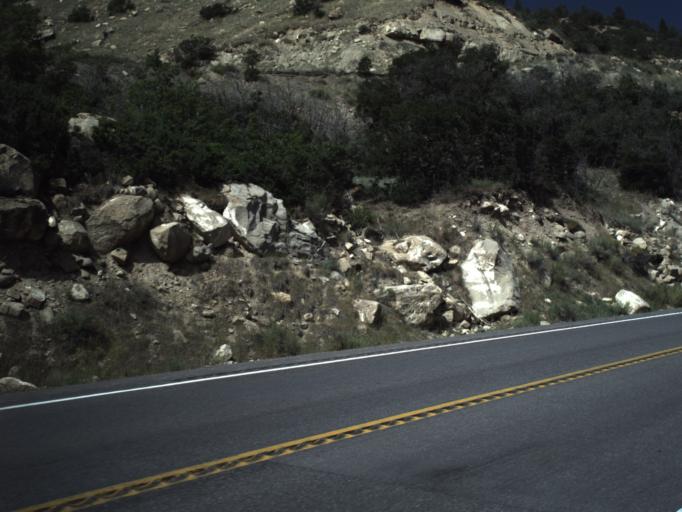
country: US
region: Utah
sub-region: Carbon County
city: Helper
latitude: 39.7771
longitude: -110.9156
